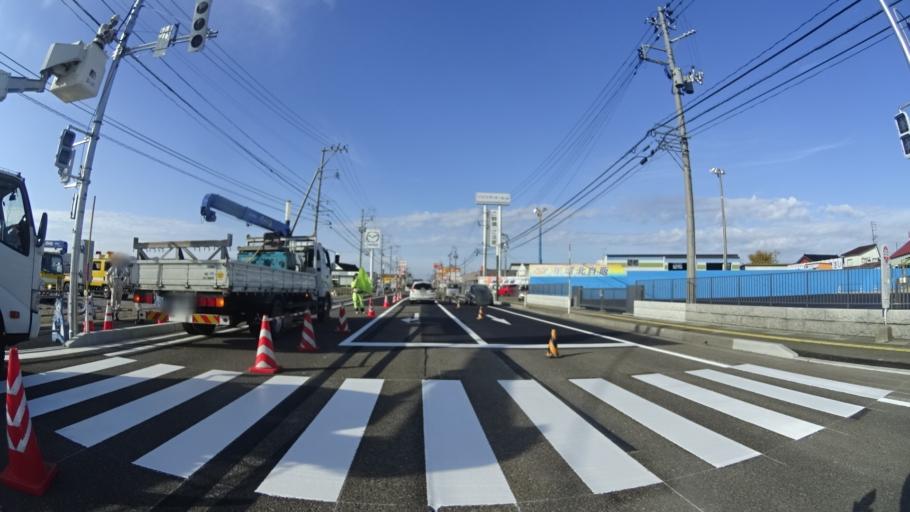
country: JP
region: Niigata
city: Joetsu
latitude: 37.1312
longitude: 138.2452
